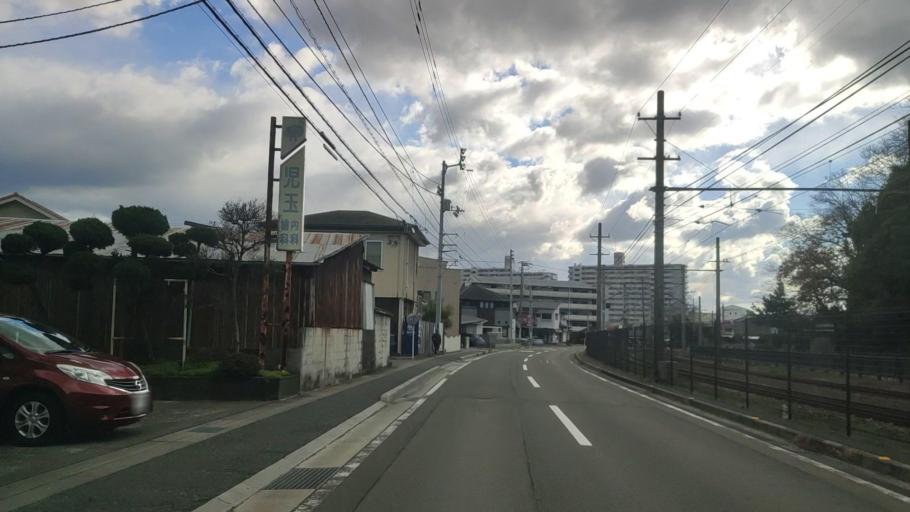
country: JP
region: Ehime
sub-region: Shikoku-chuo Shi
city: Matsuyama
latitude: 33.8694
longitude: 132.7165
